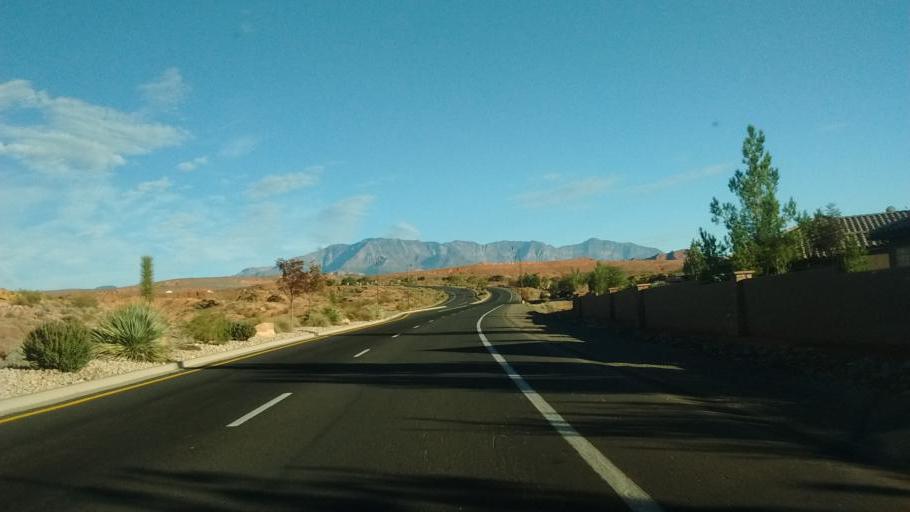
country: US
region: Utah
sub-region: Washington County
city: Washington
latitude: 37.1393
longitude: -113.4856
